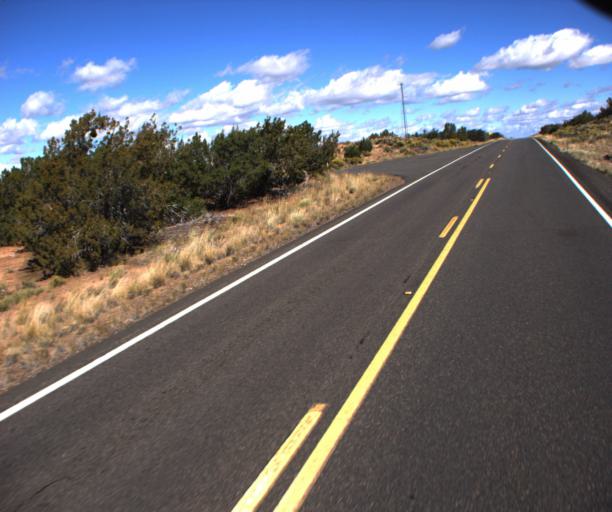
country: US
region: Arizona
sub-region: Apache County
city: Saint Johns
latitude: 34.8388
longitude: -109.2375
